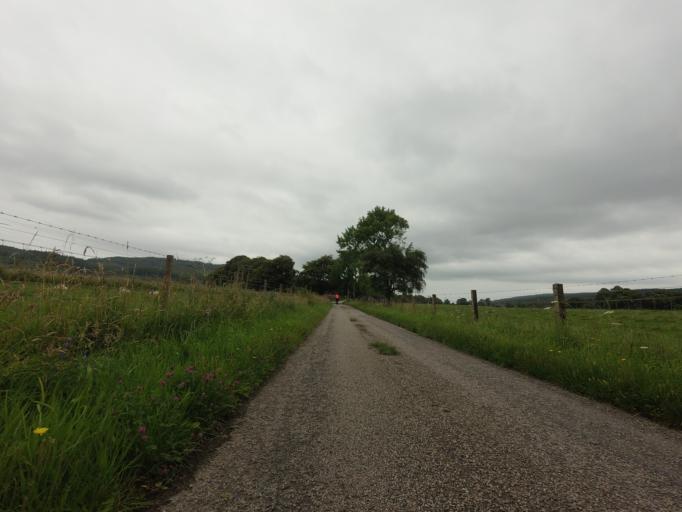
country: GB
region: Scotland
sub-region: Highland
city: Evanton
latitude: 57.9170
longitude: -4.4025
